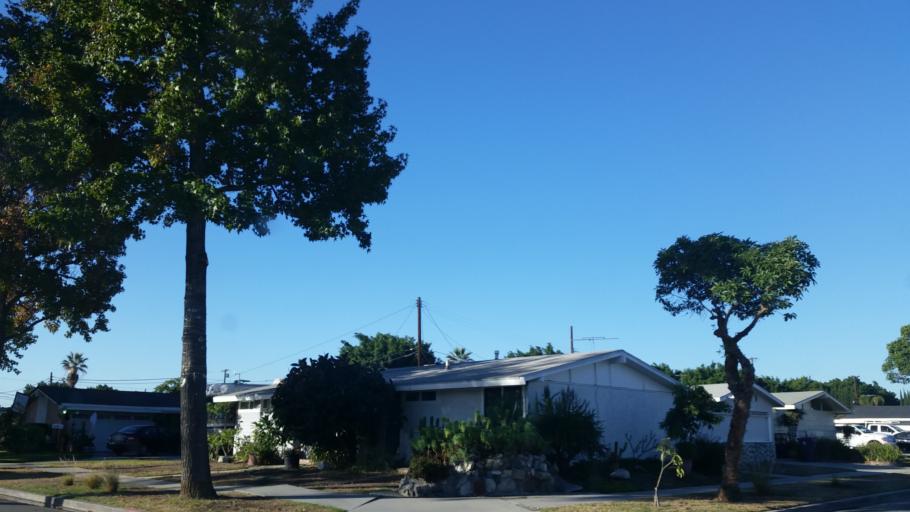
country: US
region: California
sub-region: Los Angeles County
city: Paramount
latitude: 33.8687
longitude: -118.1514
